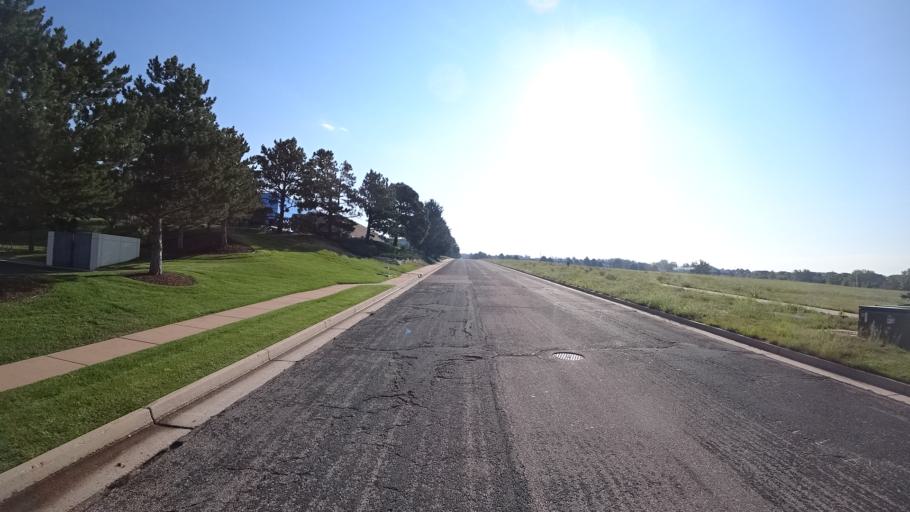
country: US
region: Colorado
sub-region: El Paso County
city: Air Force Academy
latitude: 38.9574
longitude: -104.7935
